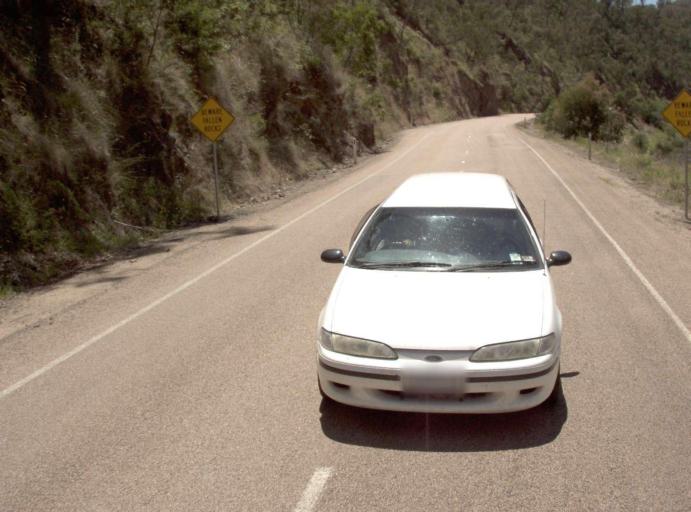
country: AU
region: Victoria
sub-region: East Gippsland
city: Bairnsdale
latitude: -37.4686
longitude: 147.8278
